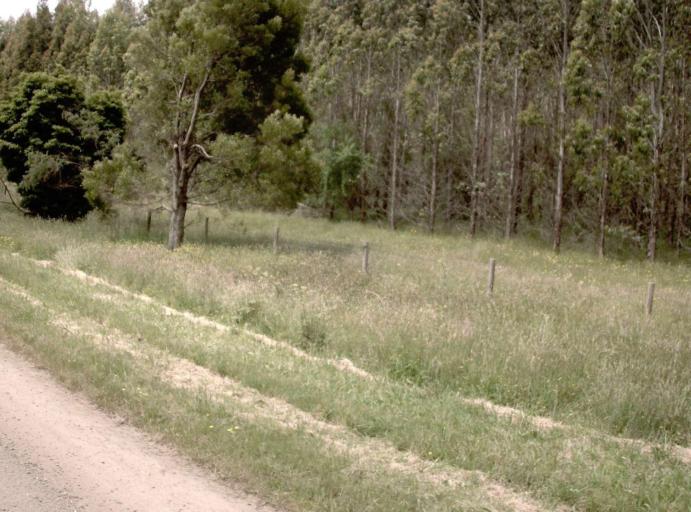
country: AU
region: Victoria
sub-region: Latrobe
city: Traralgon
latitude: -38.3945
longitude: 146.6589
